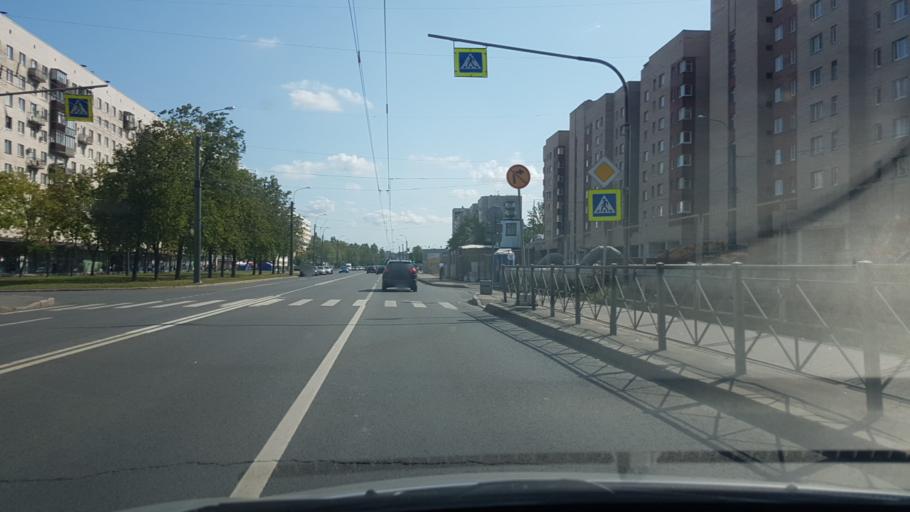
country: RU
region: St.-Petersburg
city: Sosnovaya Polyana
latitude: 59.8353
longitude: 30.1429
